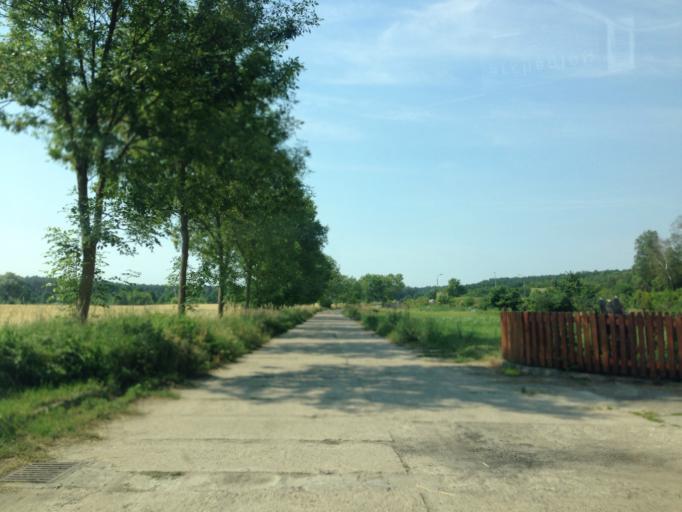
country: PL
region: Kujawsko-Pomorskie
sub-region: Powiat rypinski
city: Wapielsk
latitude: 53.2055
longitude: 19.2600
